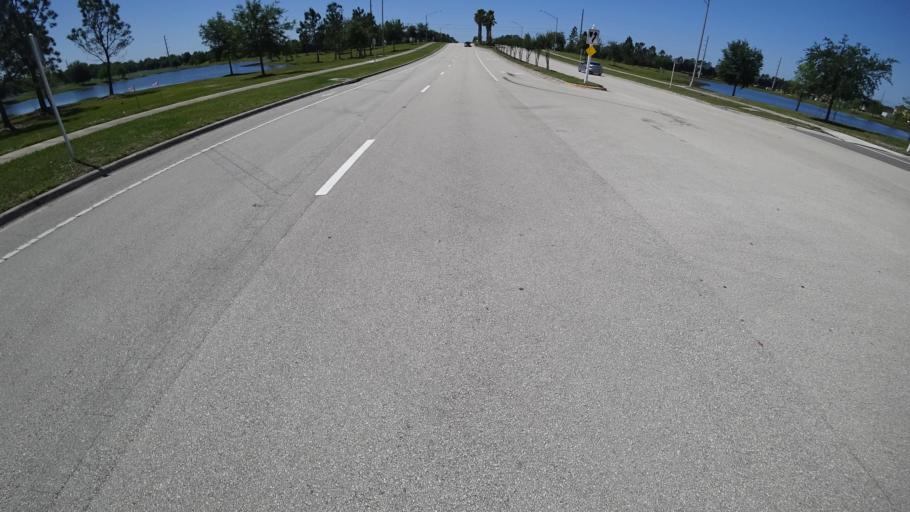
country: US
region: Florida
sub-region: Sarasota County
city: The Meadows
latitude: 27.4338
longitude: -82.3839
